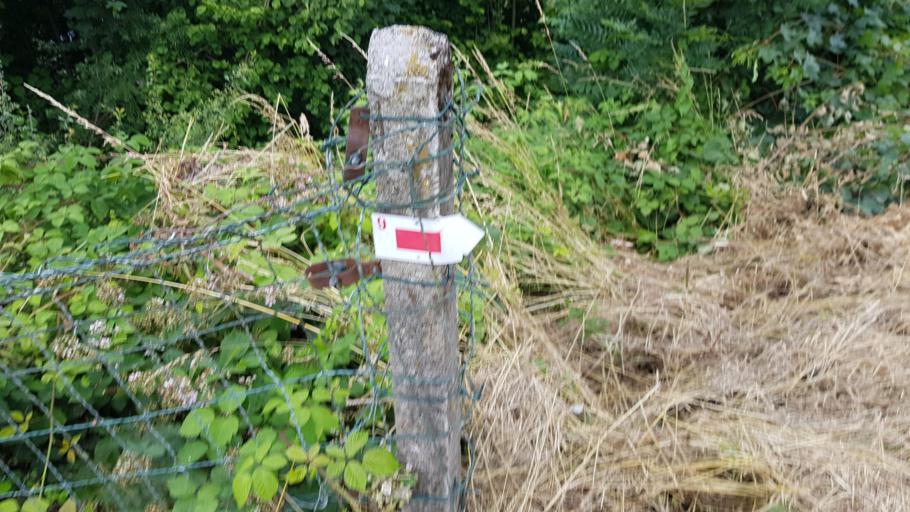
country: BE
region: Wallonia
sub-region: Province du Luxembourg
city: Bouillon
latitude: 49.7953
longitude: 5.0721
